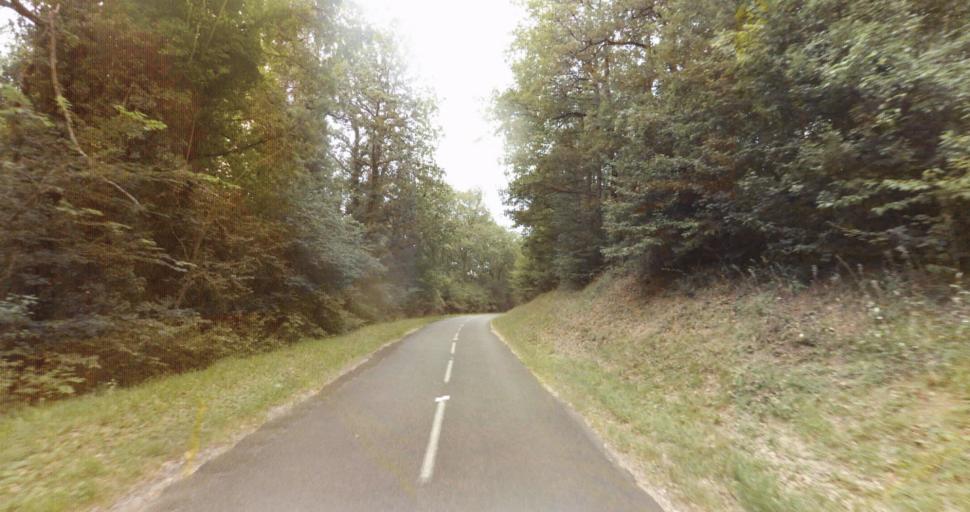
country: FR
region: Haute-Normandie
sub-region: Departement de l'Eure
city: Croth
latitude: 48.8531
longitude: 1.3659
